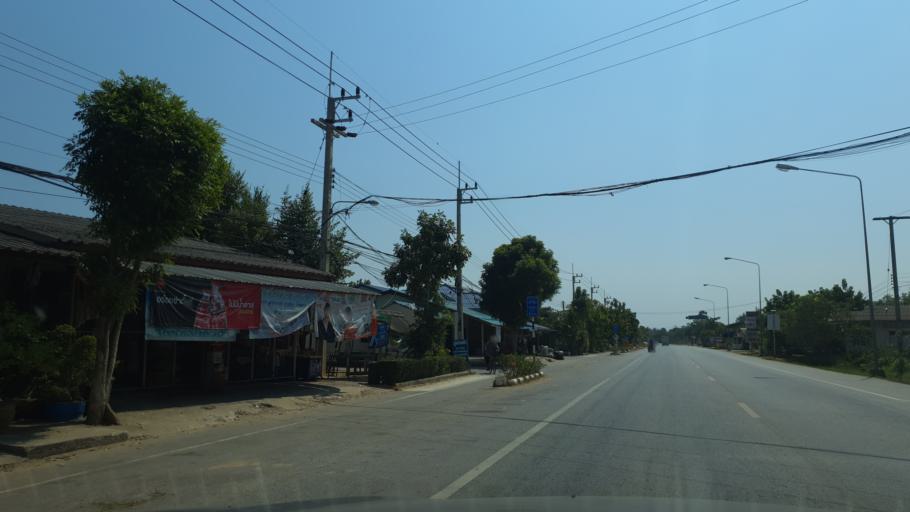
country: TH
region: Prachuap Khiri Khan
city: Pran Buri
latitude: 12.3472
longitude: 99.9412
